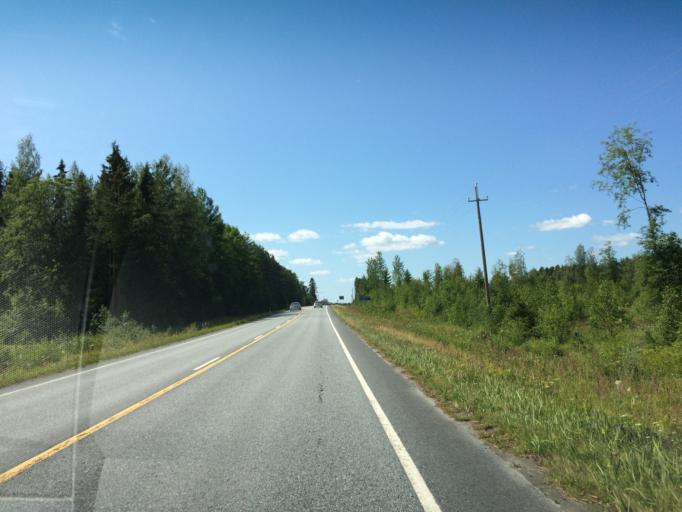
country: FI
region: Pirkanmaa
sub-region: Lounais-Pirkanmaa
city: Kiikoinen
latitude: 61.4777
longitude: 22.5846
